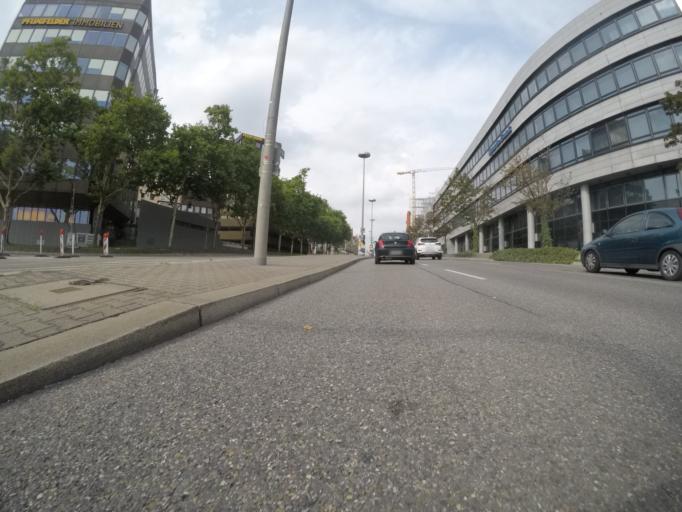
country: DE
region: Baden-Wuerttemberg
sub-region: Regierungsbezirk Stuttgart
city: Stuttgart
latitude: 48.7862
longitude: 9.1803
